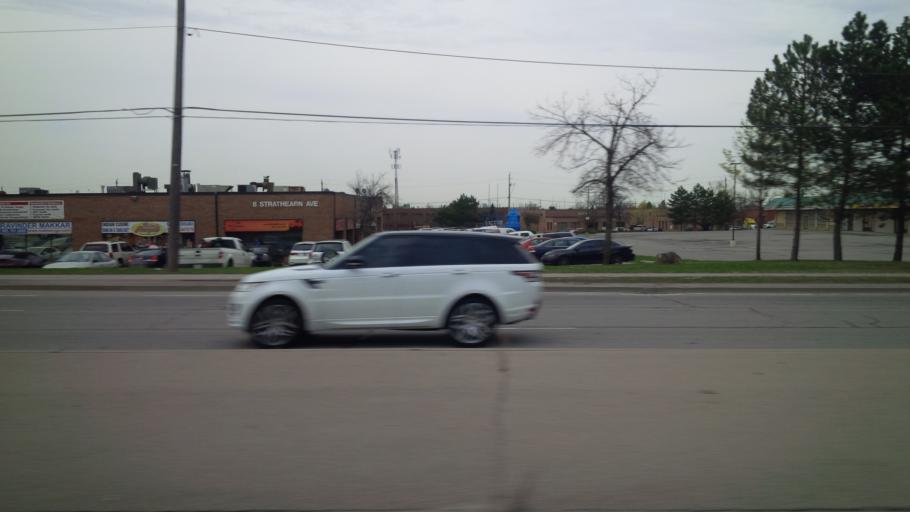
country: CA
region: Ontario
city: Brampton
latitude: 43.6923
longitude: -79.6975
